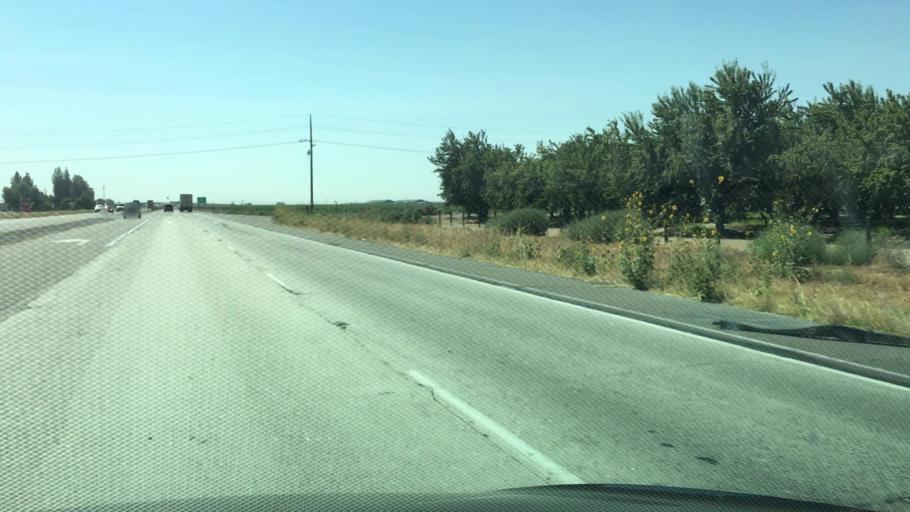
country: US
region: California
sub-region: Merced County
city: Dos Palos
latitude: 37.0836
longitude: -120.4720
